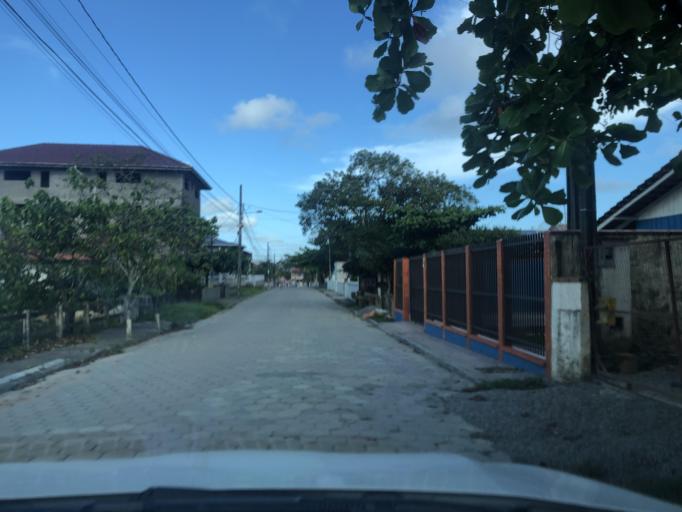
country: BR
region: Santa Catarina
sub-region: Sao Francisco Do Sul
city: Sao Francisco do Sul
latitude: -26.2252
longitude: -48.5206
